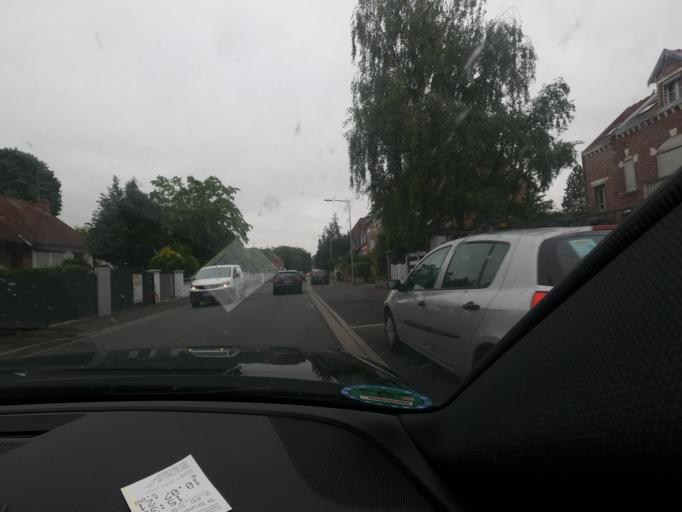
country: FR
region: Picardie
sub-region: Departement de la Somme
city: Amiens
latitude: 49.8760
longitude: 2.3061
